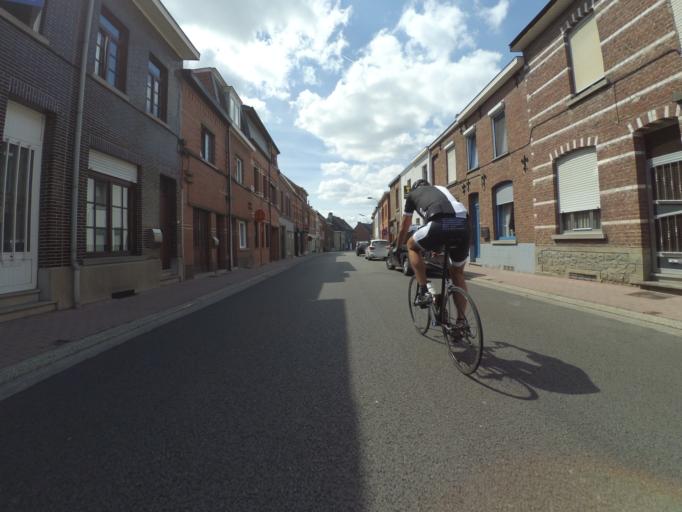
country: BE
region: Flanders
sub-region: Provincie Oost-Vlaanderen
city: Zottegem
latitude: 50.8668
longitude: 3.8066
